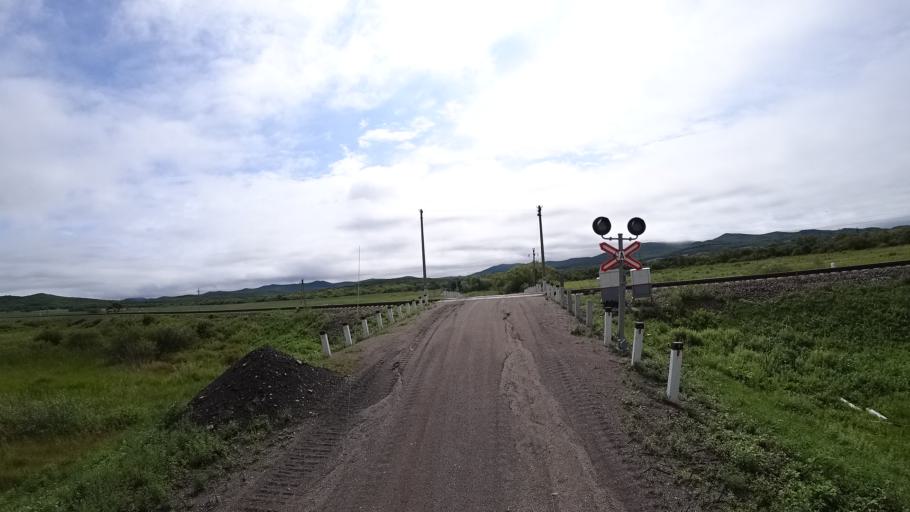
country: RU
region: Primorskiy
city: Monastyrishche
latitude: 44.1773
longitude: 132.4851
